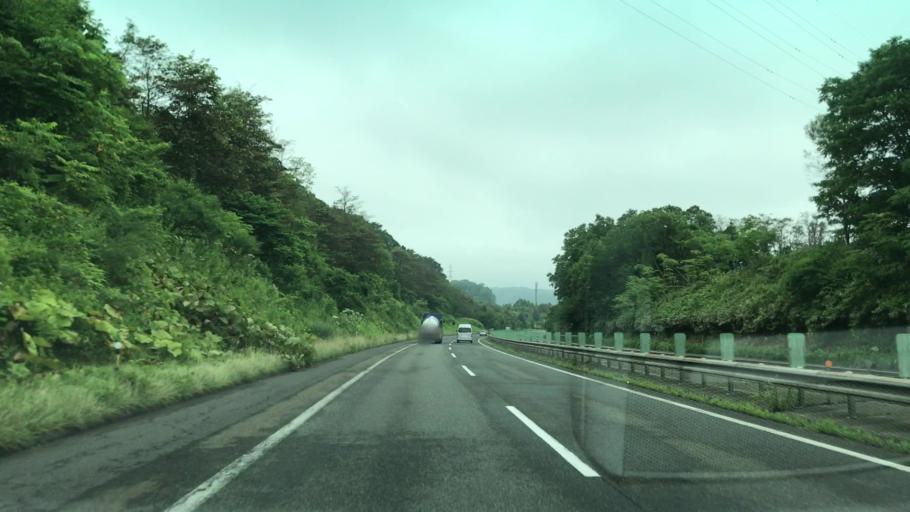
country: JP
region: Hokkaido
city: Muroran
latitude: 42.4107
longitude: 141.0795
